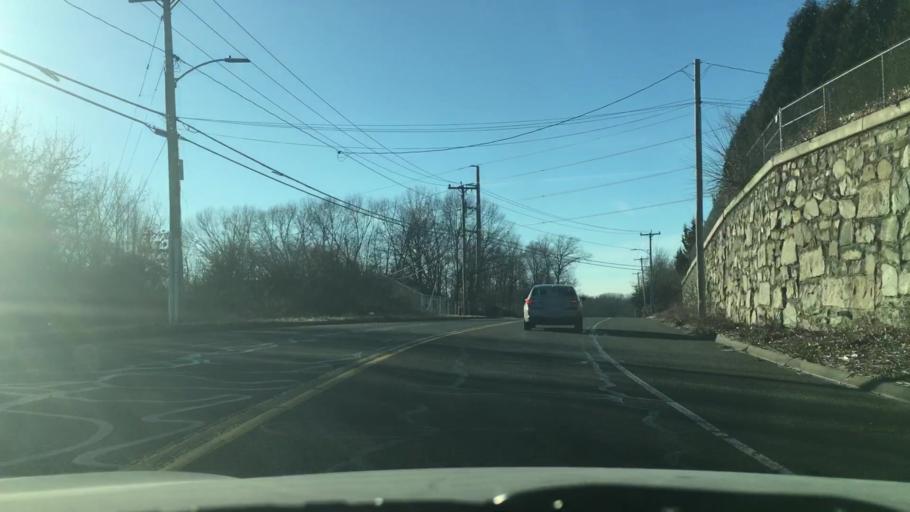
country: US
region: Massachusetts
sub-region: Hampden County
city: Ludlow
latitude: 42.1598
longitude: -72.5387
